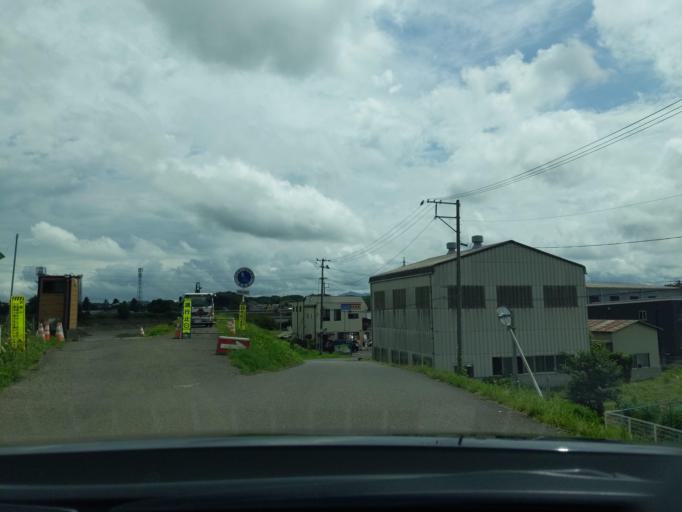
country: JP
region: Fukushima
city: Koriyama
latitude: 37.4030
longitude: 140.4015
